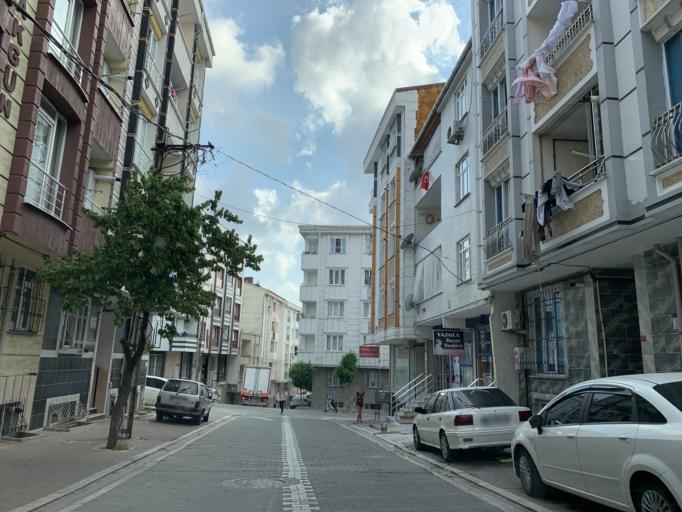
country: TR
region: Istanbul
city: Esenyurt
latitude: 41.0251
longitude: 28.6724
